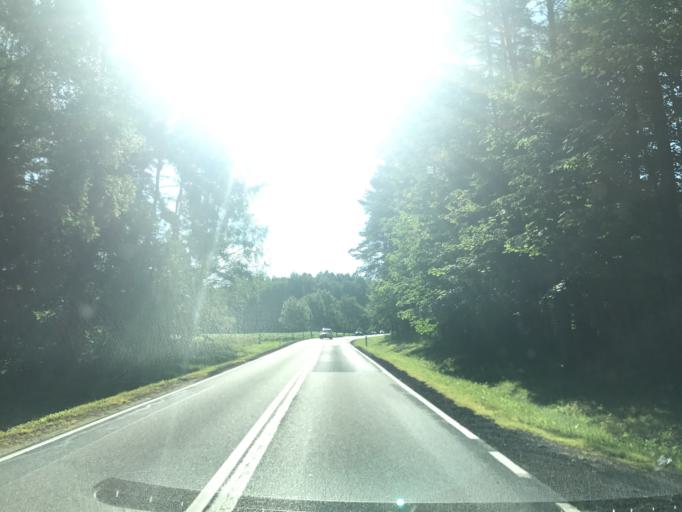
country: PL
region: Pomeranian Voivodeship
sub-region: Powiat czluchowski
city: Czluchow
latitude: 53.7028
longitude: 17.2725
